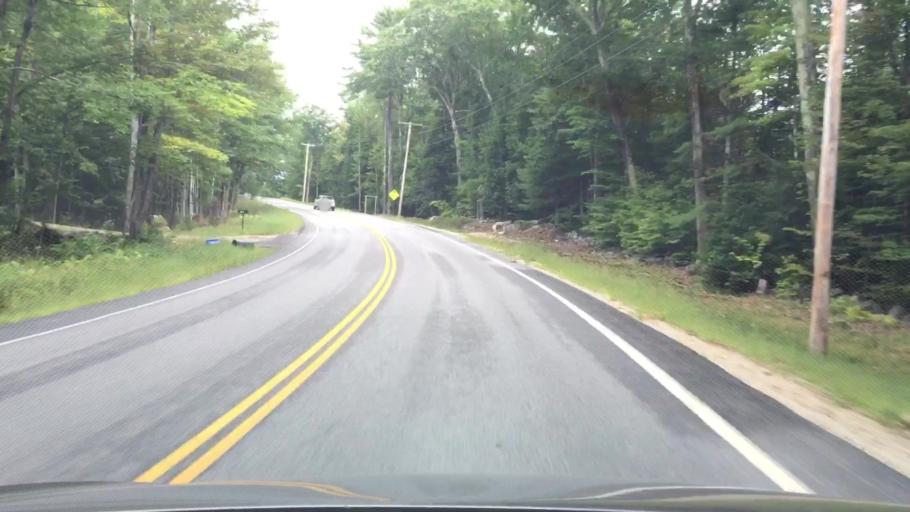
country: US
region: Maine
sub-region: Oxford County
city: Hartford
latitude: 44.3493
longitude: -70.3001
